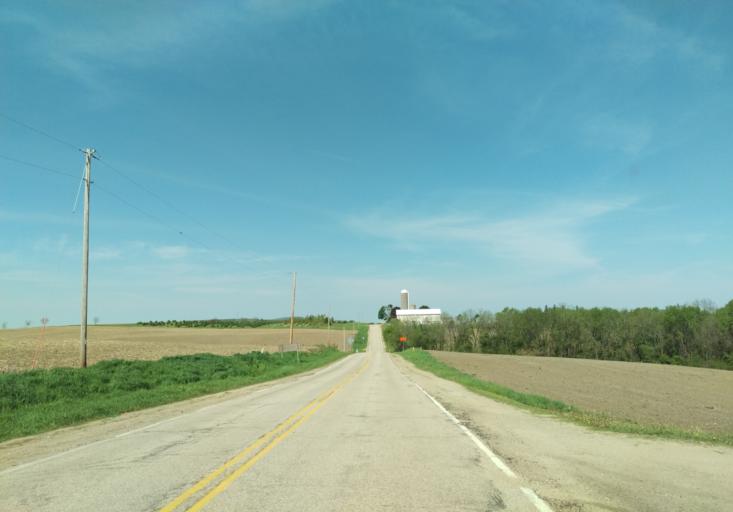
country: US
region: Wisconsin
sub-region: Dane County
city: Mount Horeb
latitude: 43.0412
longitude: -89.7307
